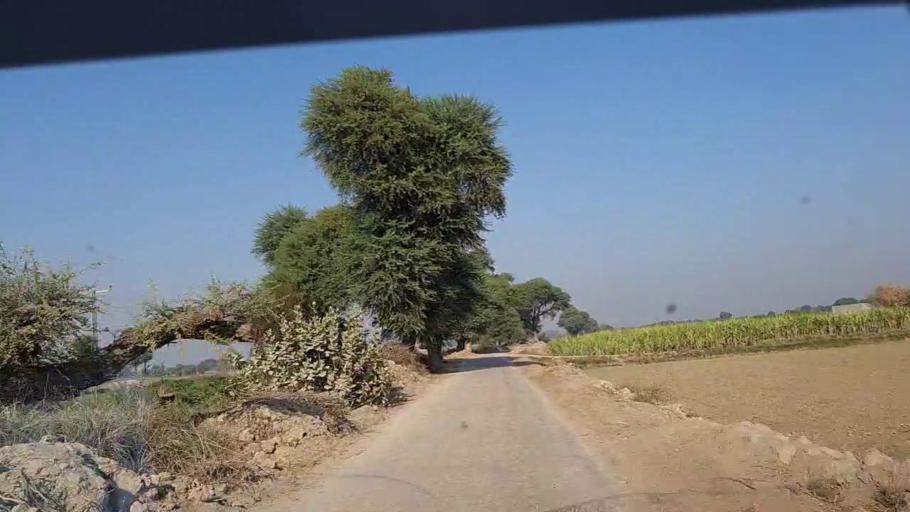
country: PK
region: Sindh
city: Sobhadero
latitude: 27.2425
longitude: 68.3223
